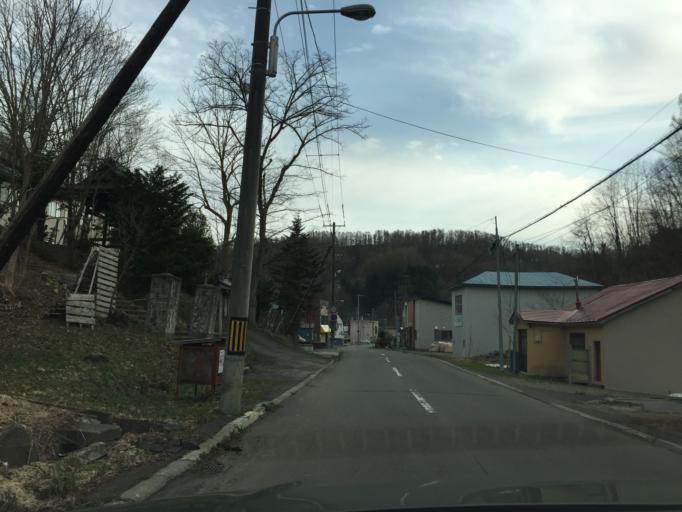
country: JP
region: Hokkaido
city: Utashinai
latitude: 43.5243
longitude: 142.0413
